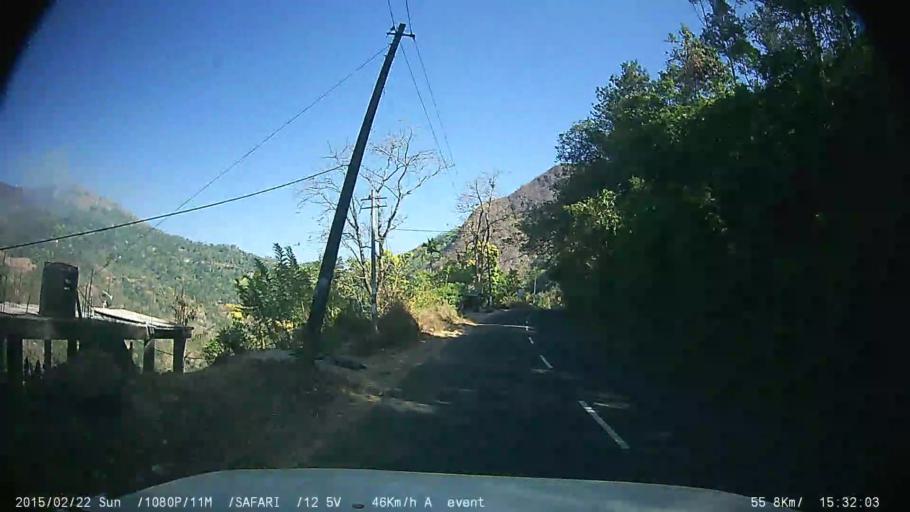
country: IN
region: Kerala
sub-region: Kottayam
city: Erattupetta
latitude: 9.5587
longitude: 76.9597
